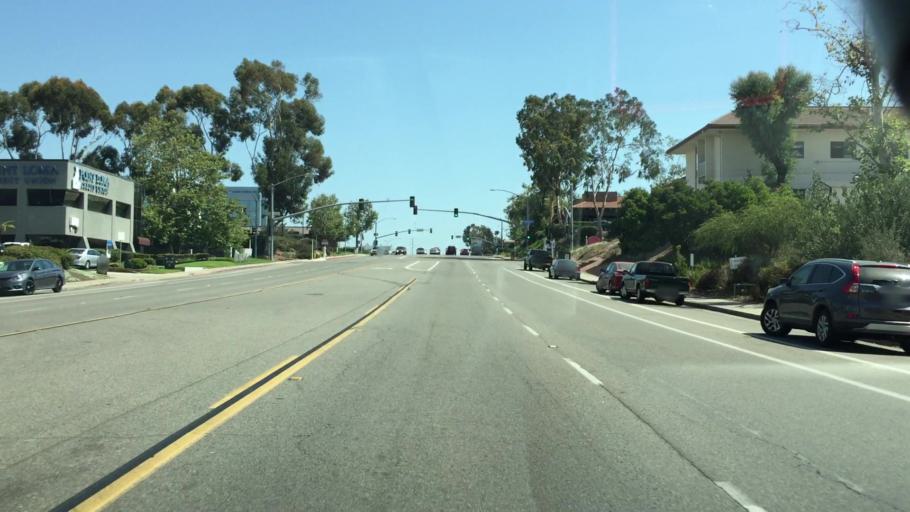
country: US
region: California
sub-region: San Diego County
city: San Diego
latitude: 32.8339
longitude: -117.1268
